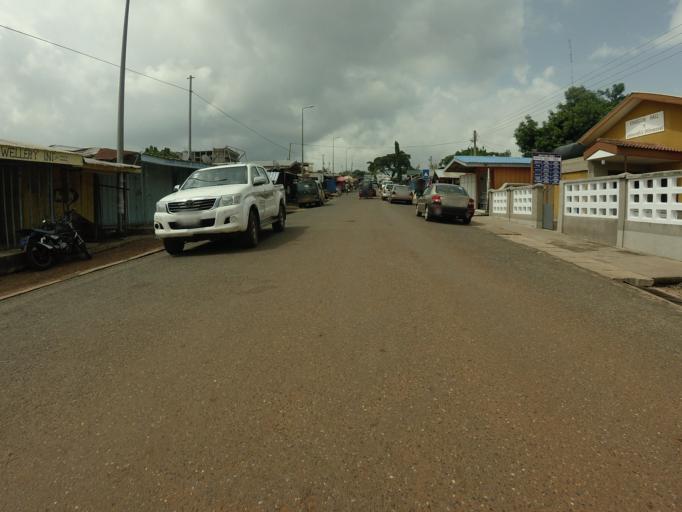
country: GH
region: Volta
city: Ho
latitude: 6.6161
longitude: 0.4715
